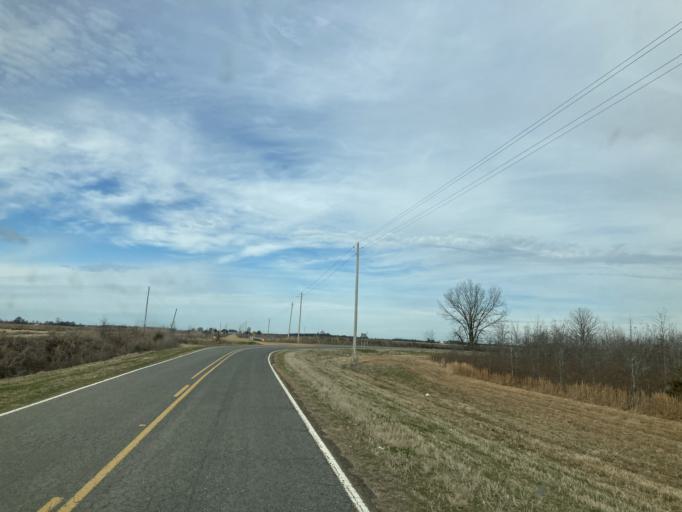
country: US
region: Mississippi
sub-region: Humphreys County
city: Belzoni
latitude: 33.1666
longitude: -90.5722
